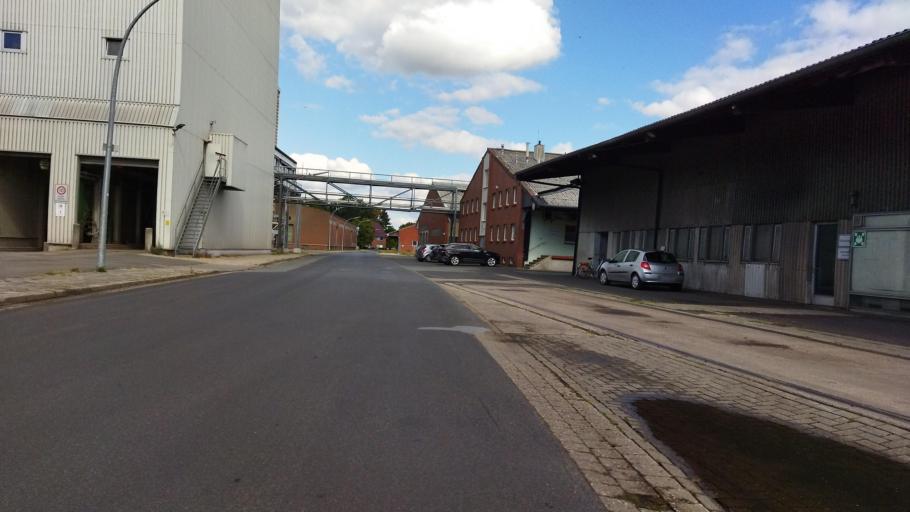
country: DE
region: Lower Saxony
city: Lingen
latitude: 52.5036
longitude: 7.3078
